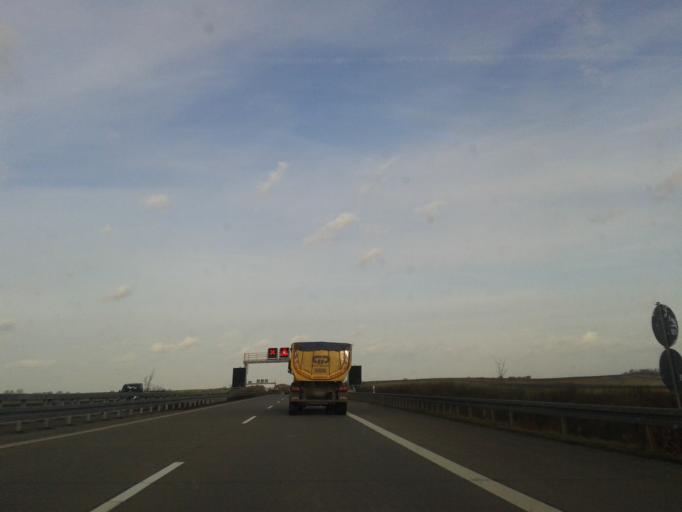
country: DE
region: Saxony-Anhalt
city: Welsleben
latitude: 52.0083
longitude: 11.6569
